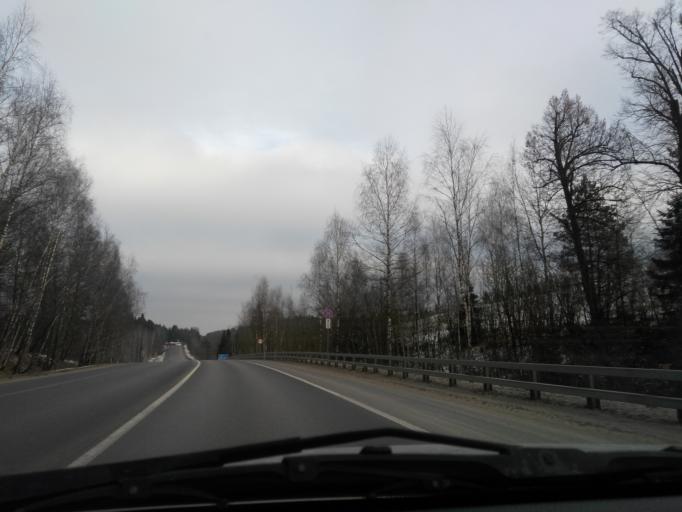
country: RU
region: Moskovskaya
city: Troitsk
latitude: 55.2752
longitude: 37.1364
